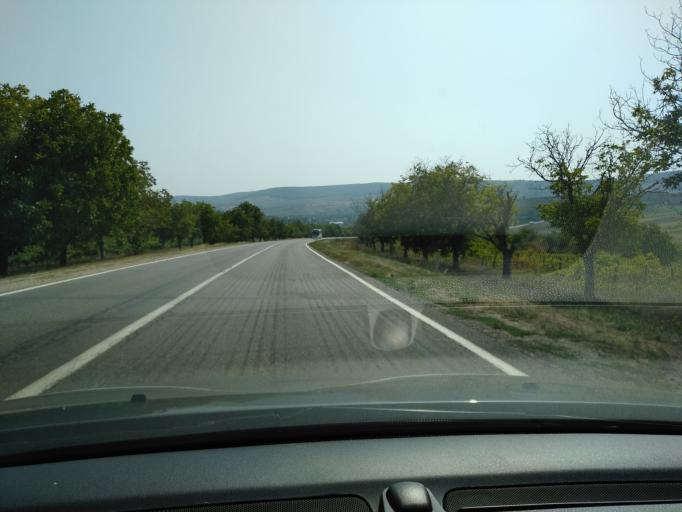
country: MD
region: Nisporeni
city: Nisporeni
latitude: 47.0412
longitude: 28.2853
